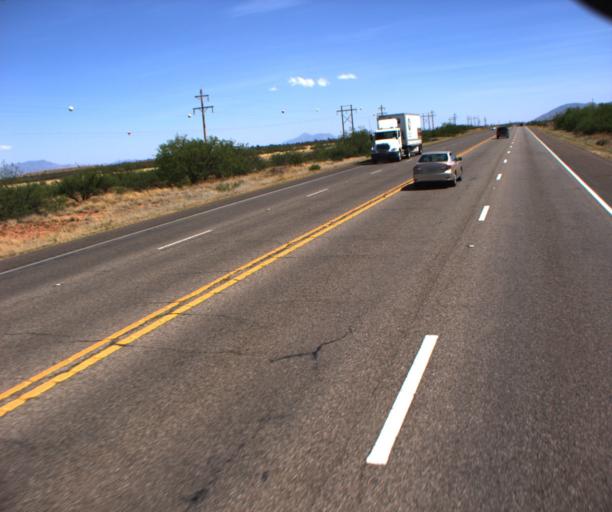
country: US
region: Arizona
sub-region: Cochise County
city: Sierra Vista
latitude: 31.5866
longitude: -110.3211
